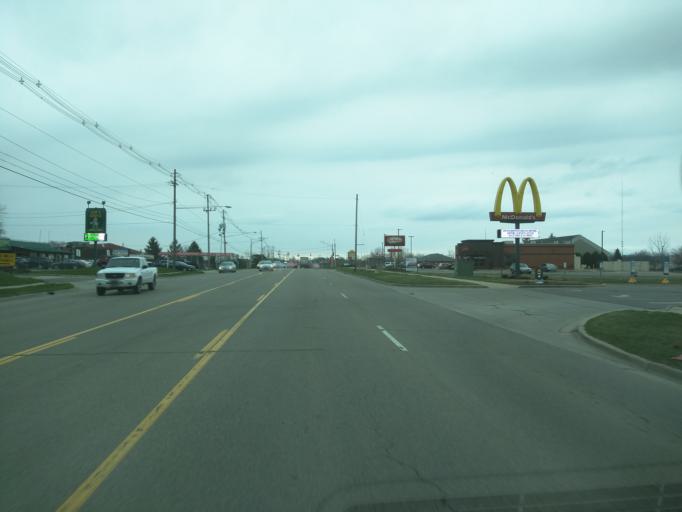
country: US
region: Michigan
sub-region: Ingham County
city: Holt
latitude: 42.6829
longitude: -84.5160
